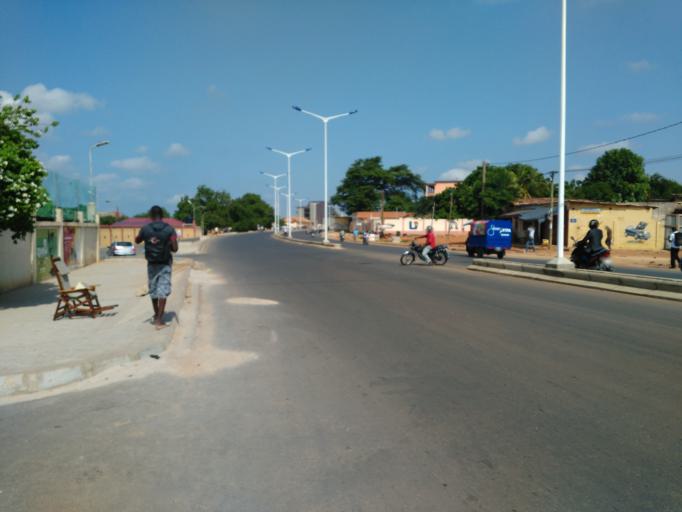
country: TG
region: Maritime
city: Lome
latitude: 6.1500
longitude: 1.2349
